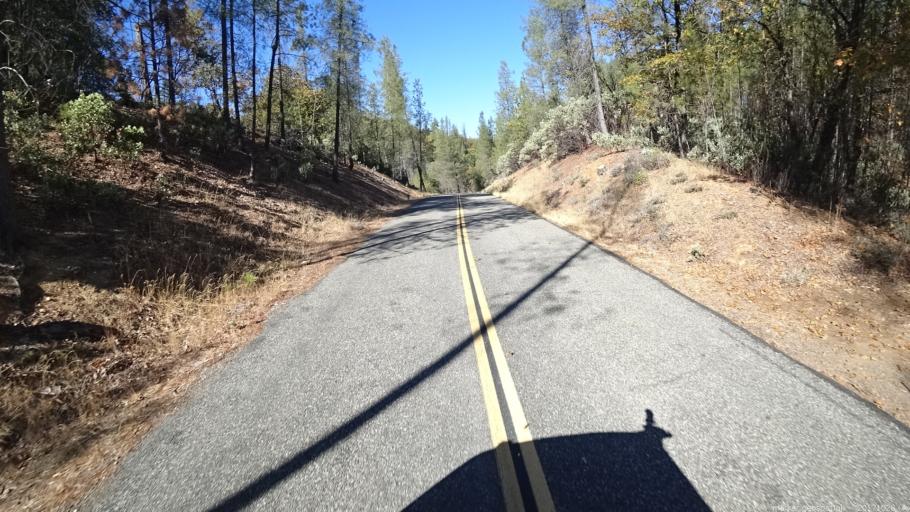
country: US
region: California
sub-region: Shasta County
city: Shasta
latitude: 40.6139
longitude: -122.5772
